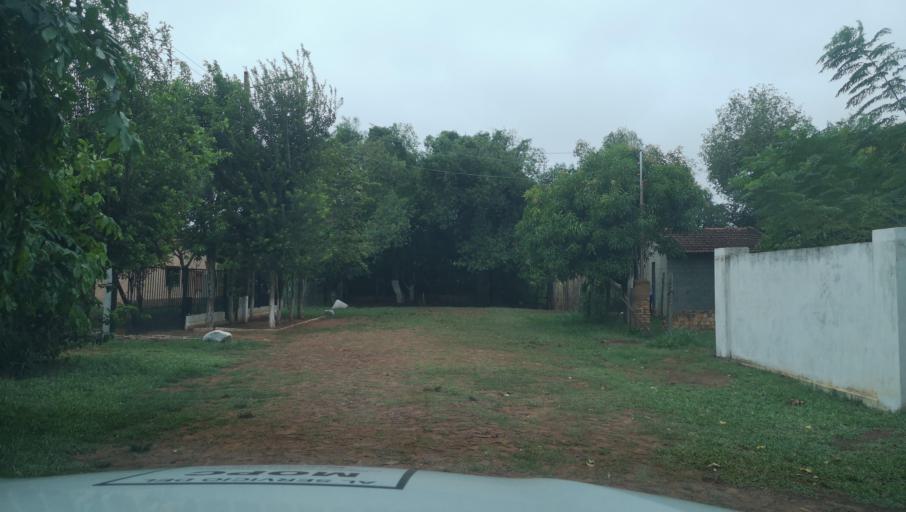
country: PY
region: Misiones
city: Santa Maria
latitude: -26.8984
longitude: -57.0337
